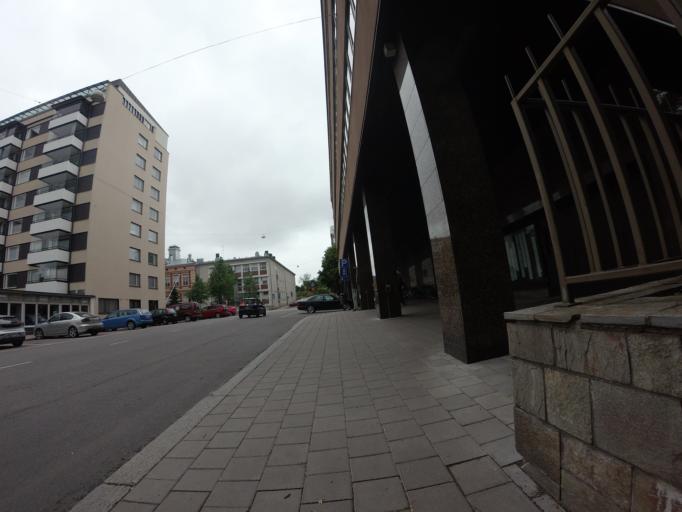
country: FI
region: Varsinais-Suomi
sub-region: Turku
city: Turku
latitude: 60.4522
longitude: 22.2620
